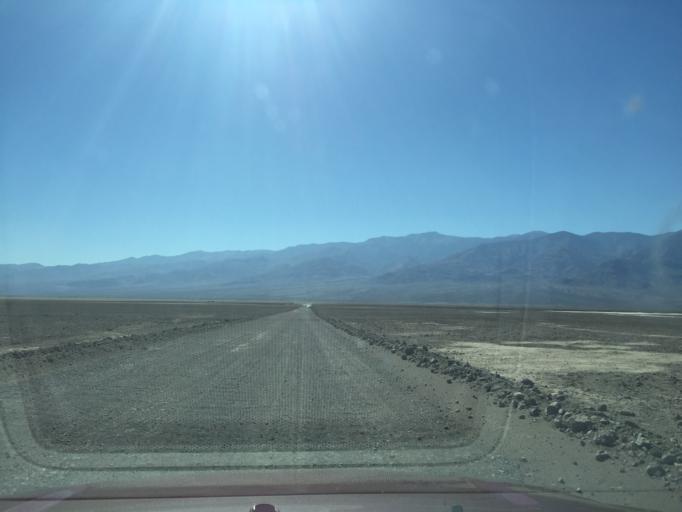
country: US
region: Nevada
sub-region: Nye County
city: Beatty
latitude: 36.2953
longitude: -116.8165
